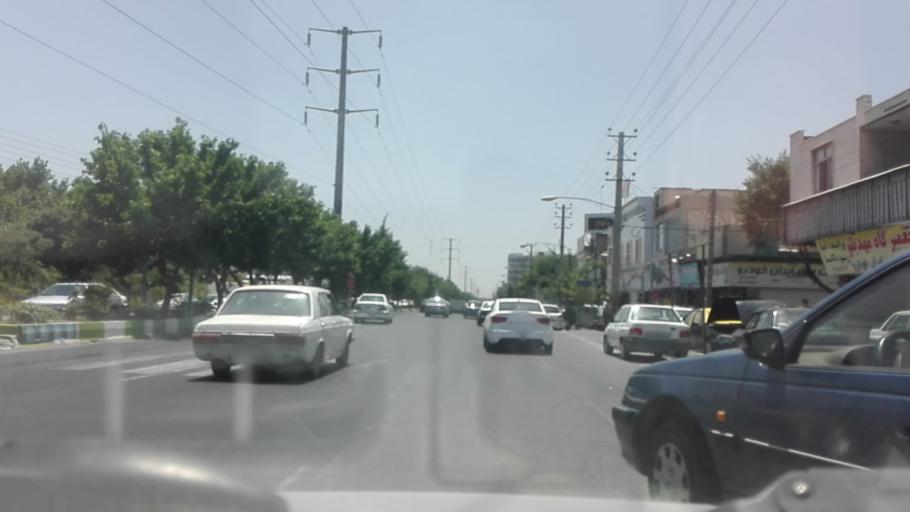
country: IR
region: Tehran
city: Shahre Jadide Andisheh
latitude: 35.7187
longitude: 50.9935
